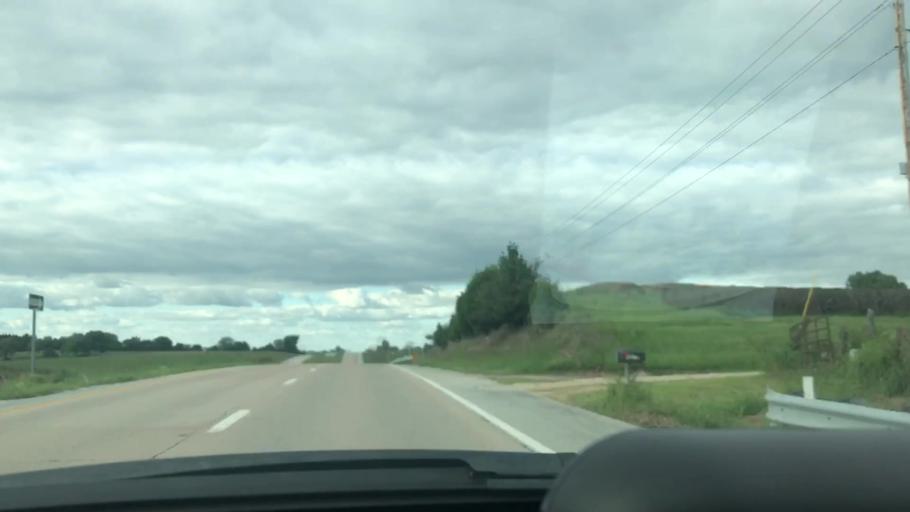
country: US
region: Missouri
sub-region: Benton County
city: Lincoln
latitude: 38.3226
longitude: -93.3420
